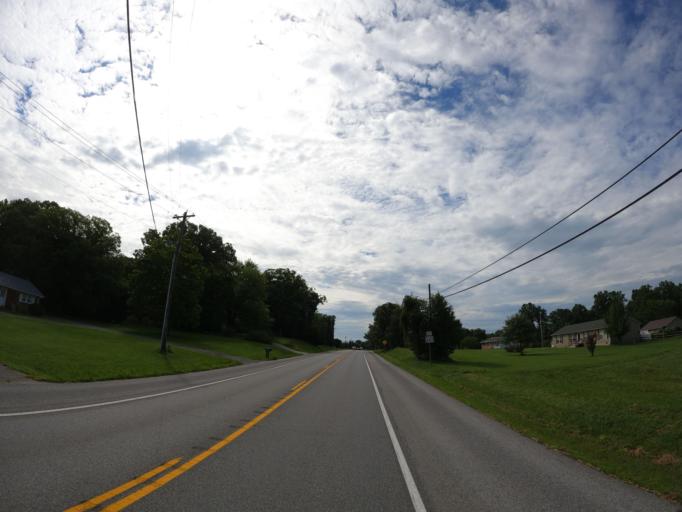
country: US
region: Maryland
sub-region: Saint Mary's County
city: Leonardtown
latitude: 38.3672
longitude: -76.6851
